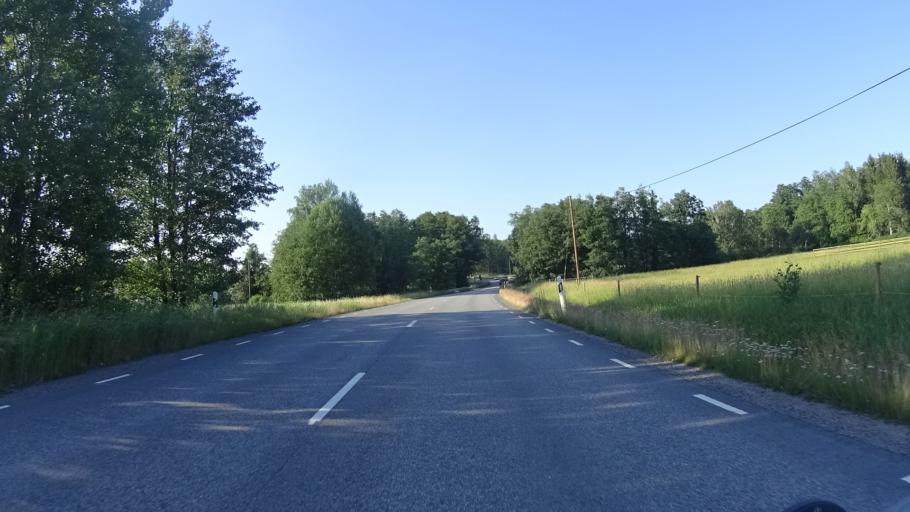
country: SE
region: Stockholm
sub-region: Sodertalje Kommun
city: Pershagen
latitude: 59.1400
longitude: 17.6490
